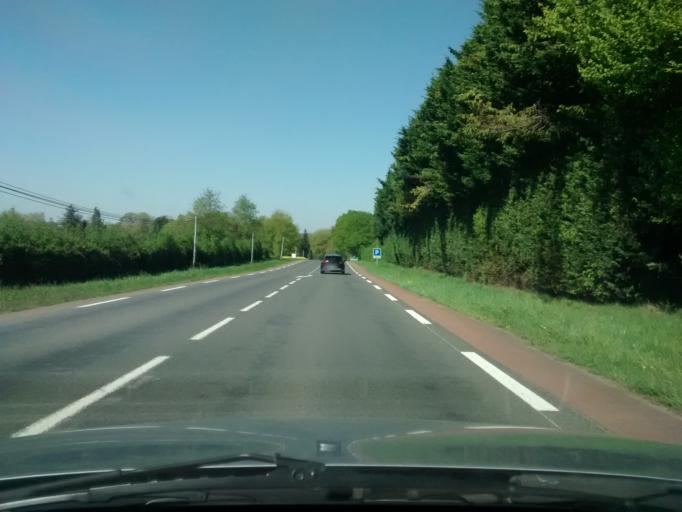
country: FR
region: Pays de la Loire
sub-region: Departement de la Sarthe
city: Brulon
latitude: 48.0298
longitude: -0.2782
